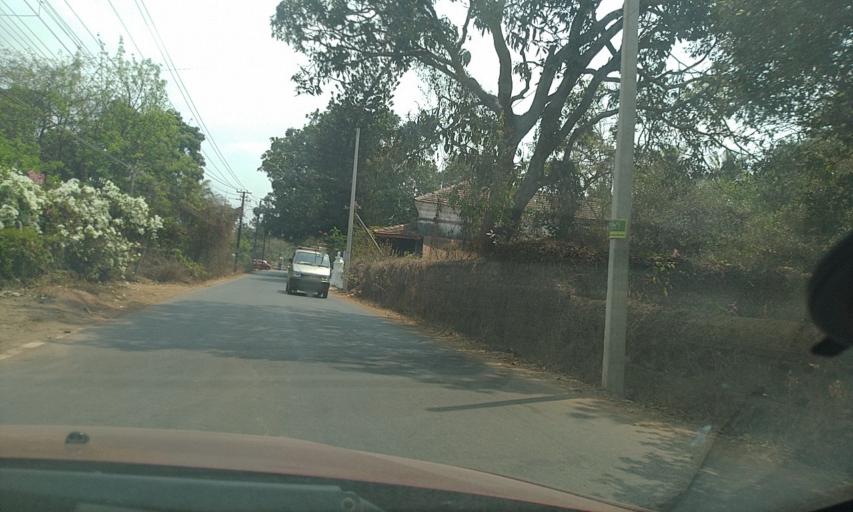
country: IN
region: Goa
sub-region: North Goa
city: Solim
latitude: 15.5907
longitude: 73.7698
